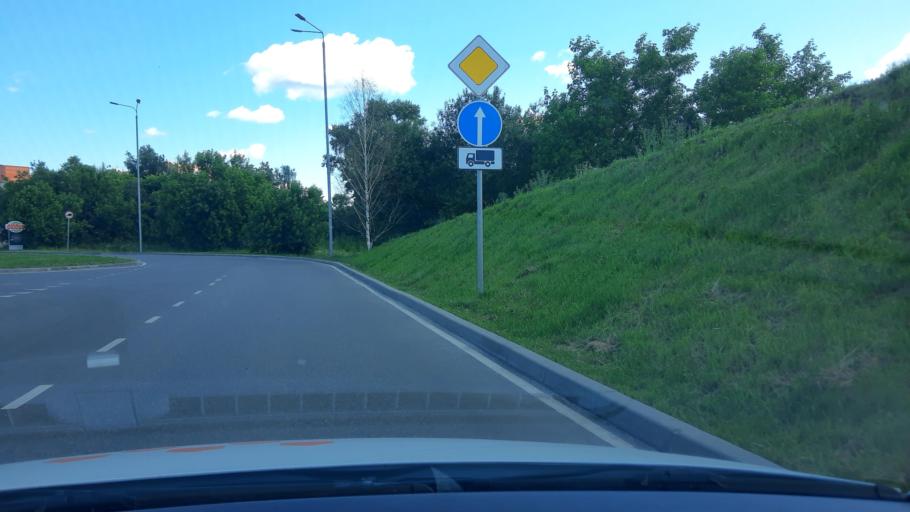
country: RU
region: Moskovskaya
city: Balashikha
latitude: 55.7933
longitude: 37.9484
